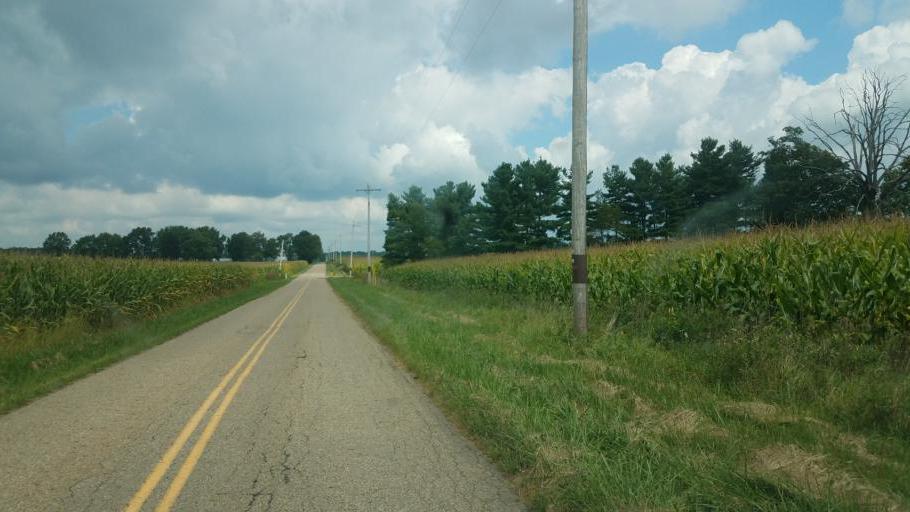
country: US
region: Ohio
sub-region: Licking County
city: Utica
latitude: 40.2873
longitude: -82.4897
